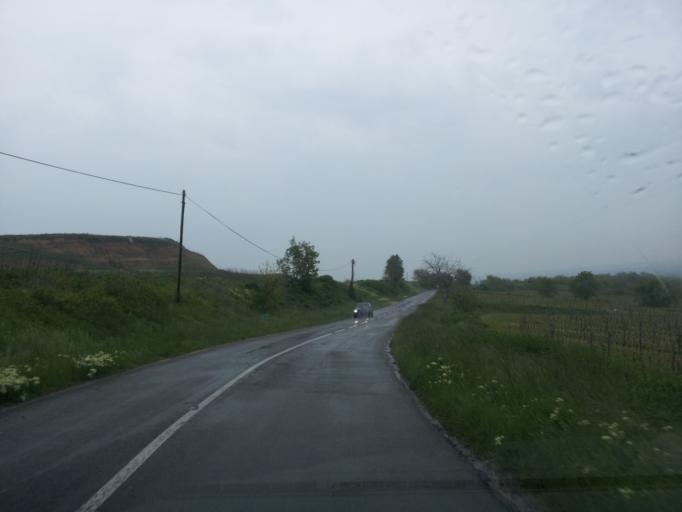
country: HU
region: Tolna
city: Szekszard
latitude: 46.2895
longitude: 18.6742
